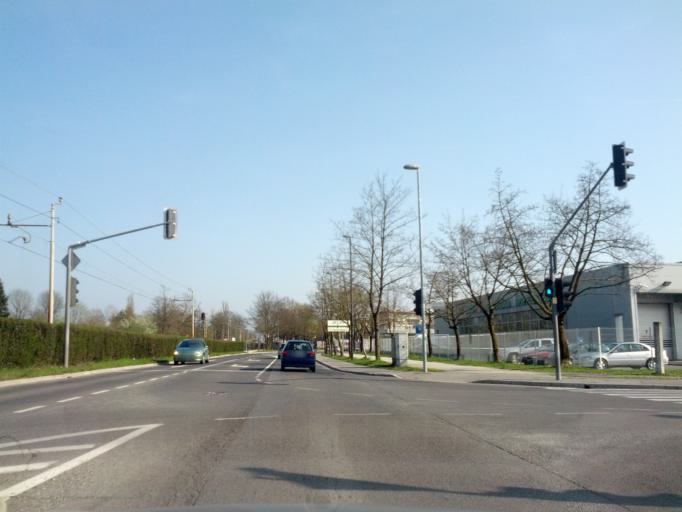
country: SI
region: Ljubljana
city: Ljubljana
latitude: 46.0794
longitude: 14.4874
